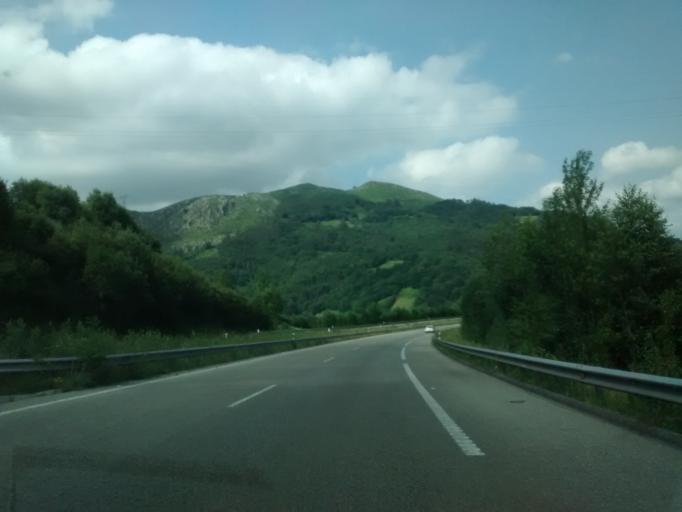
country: ES
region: Asturias
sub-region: Province of Asturias
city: Sama
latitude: 43.3187
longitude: -5.7448
